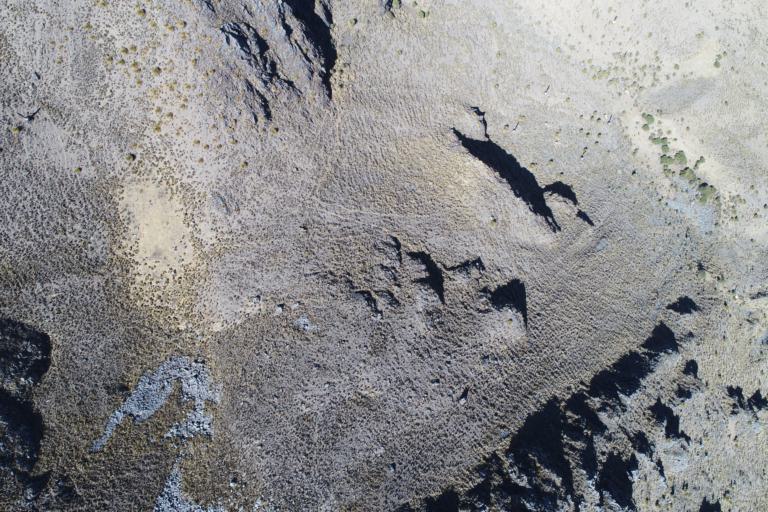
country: BO
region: La Paz
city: Viloco
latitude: -16.8082
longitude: -67.5470
